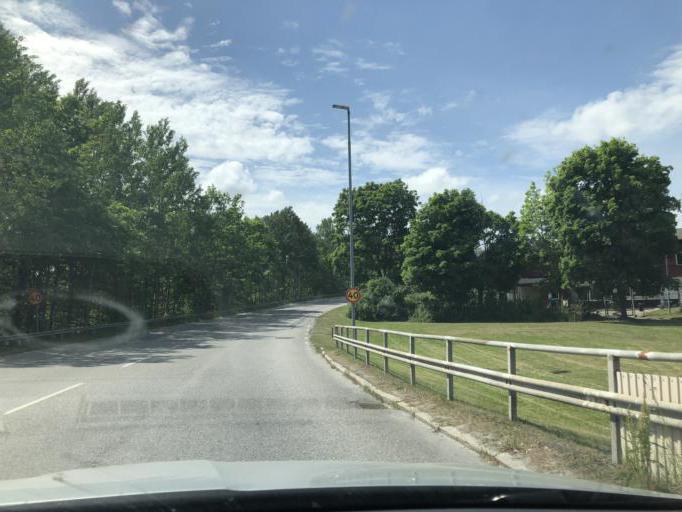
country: SE
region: Stockholm
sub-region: Botkyrka Kommun
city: Alby
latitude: 59.2410
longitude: 17.8542
